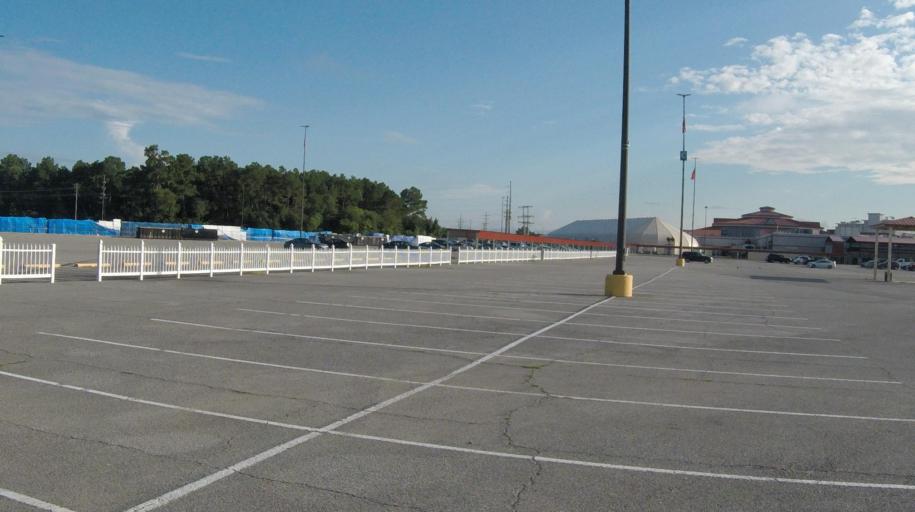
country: US
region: Louisiana
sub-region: Allen Parish
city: Kinder
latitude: 30.5433
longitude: -92.8163
